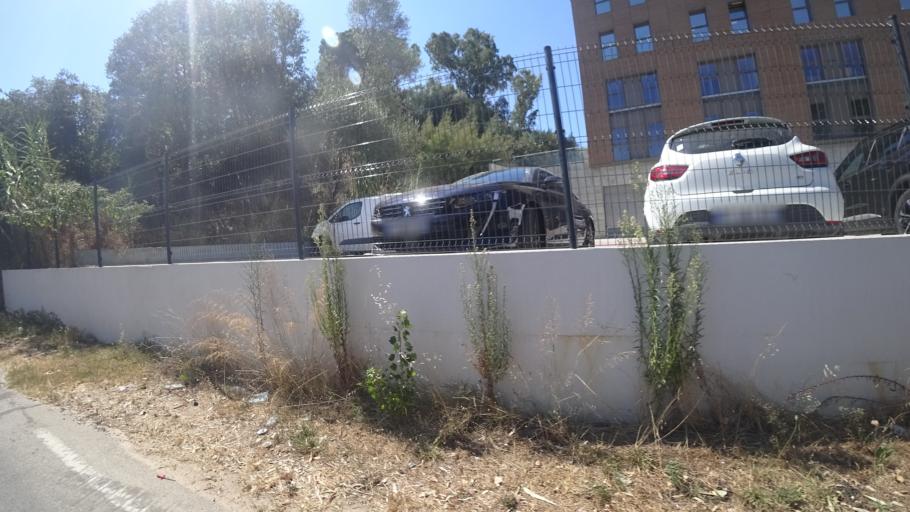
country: FR
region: Corsica
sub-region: Departement de la Corse-du-Sud
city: Ajaccio
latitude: 41.9382
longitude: 8.7374
